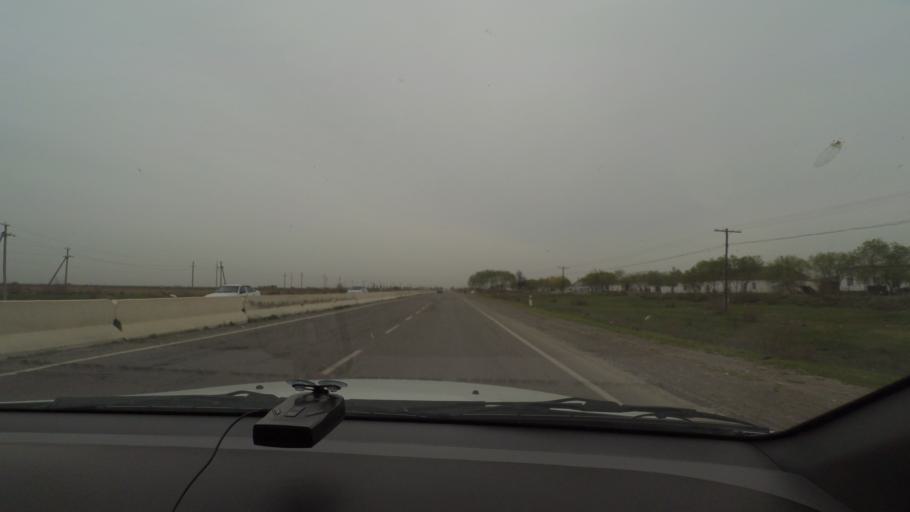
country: UZ
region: Sirdaryo
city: Guliston
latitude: 40.4956
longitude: 68.6329
